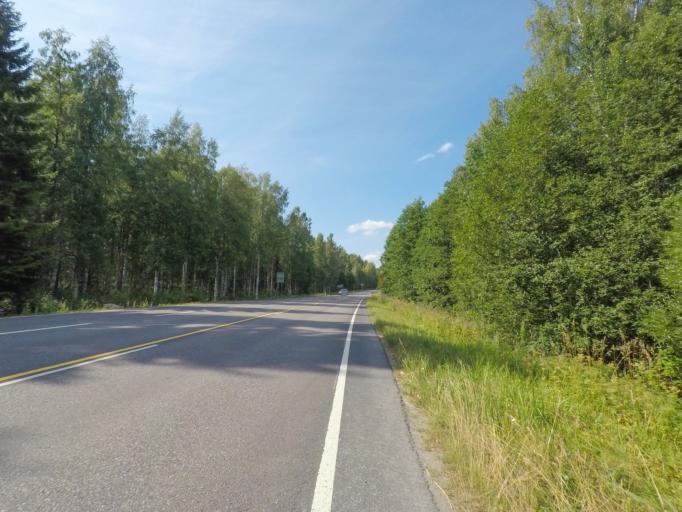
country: FI
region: Southern Savonia
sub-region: Mikkeli
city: Puumala
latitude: 61.5114
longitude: 28.1800
